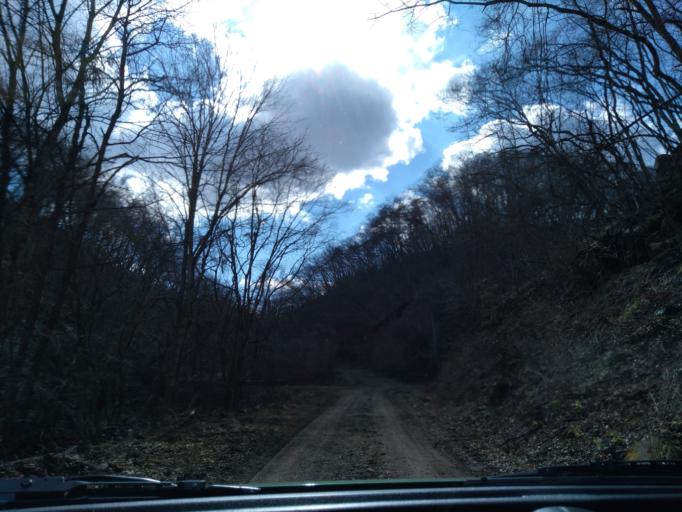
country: JP
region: Iwate
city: Ichinoseki
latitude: 38.9854
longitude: 141.0245
